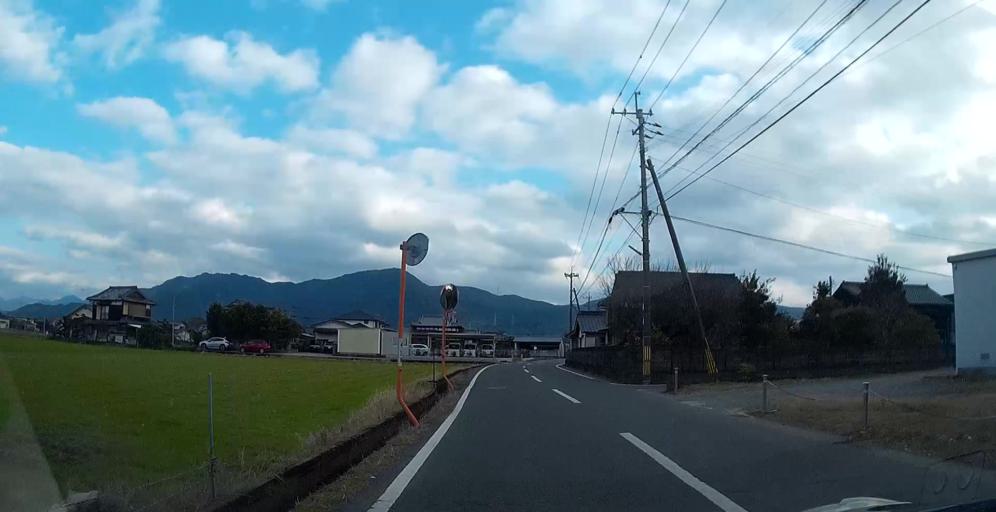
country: JP
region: Kumamoto
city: Yatsushiro
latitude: 32.5328
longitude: 130.6366
